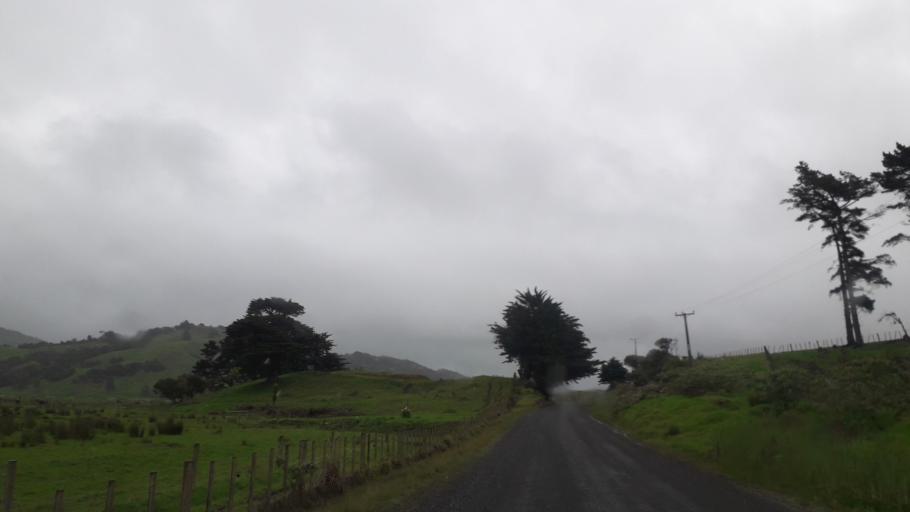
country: NZ
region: Northland
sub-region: Far North District
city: Ahipara
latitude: -35.4183
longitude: 173.3627
